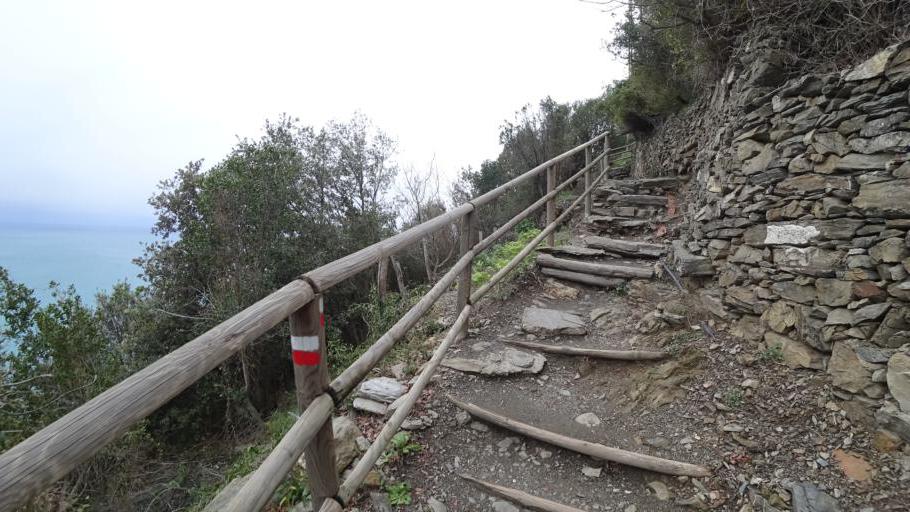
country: IT
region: Liguria
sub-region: Provincia di La Spezia
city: Vernazza
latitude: 44.1288
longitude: 9.7013
